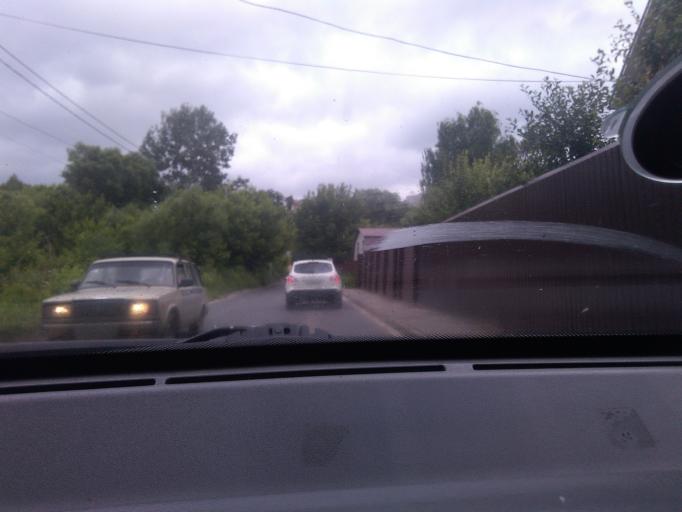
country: RU
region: Kursk
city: Kursk
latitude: 51.7388
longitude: 36.1785
